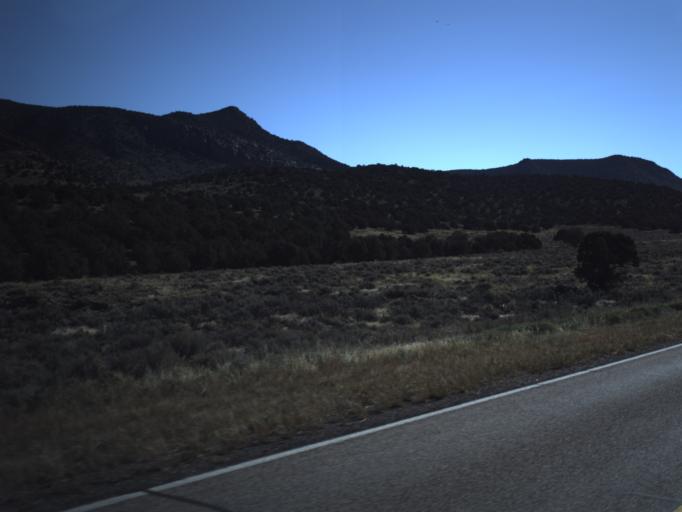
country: US
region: Utah
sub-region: Washington County
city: Enterprise
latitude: 37.6740
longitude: -113.4917
